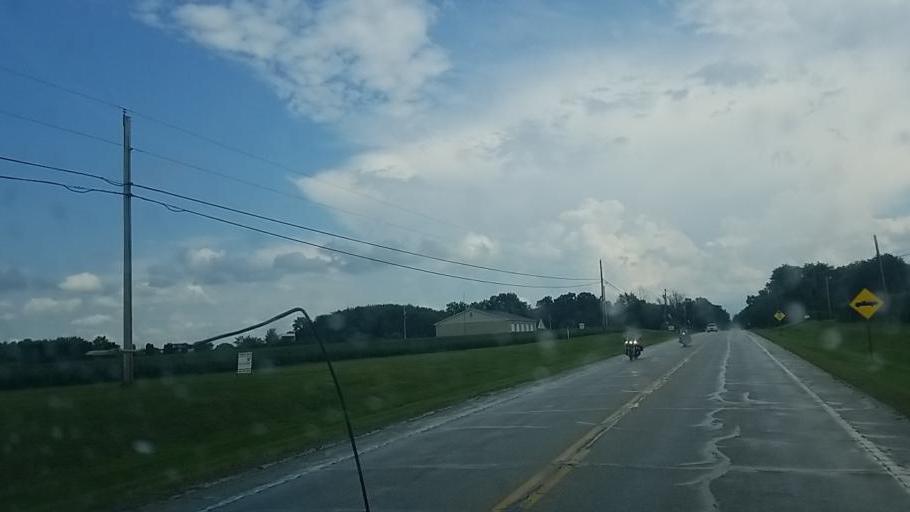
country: US
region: Ohio
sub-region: Lorain County
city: Grafton
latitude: 41.1680
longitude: -82.0342
